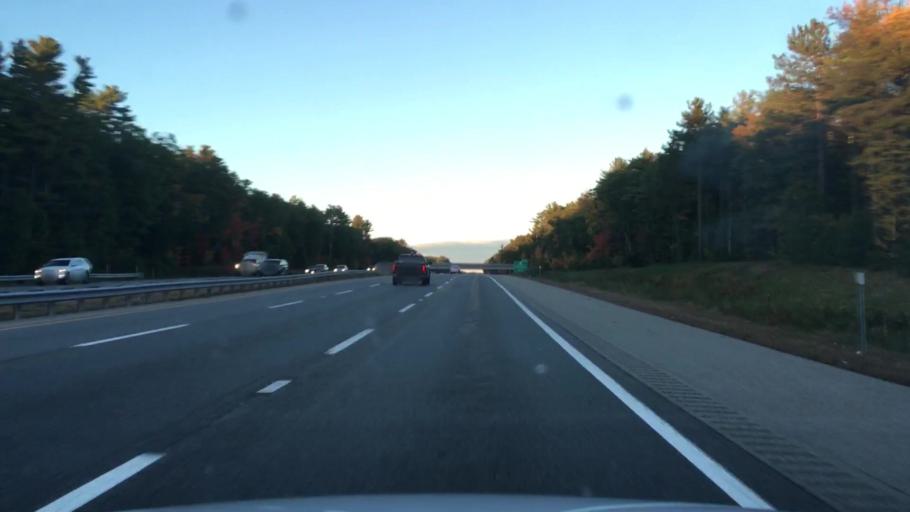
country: US
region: Maine
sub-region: York County
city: West Kennebunk
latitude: 43.3773
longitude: -70.5779
